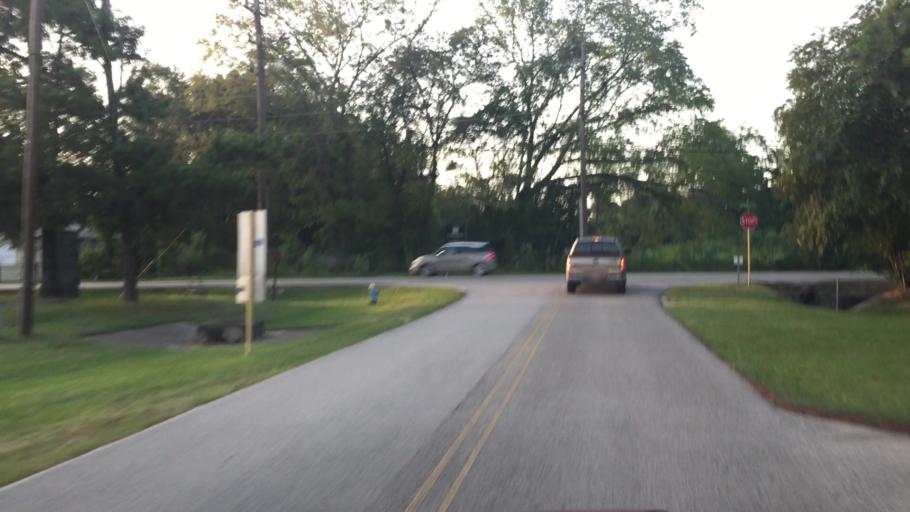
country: US
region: Texas
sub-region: Harris County
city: Hudson
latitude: 30.0009
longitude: -95.5151
